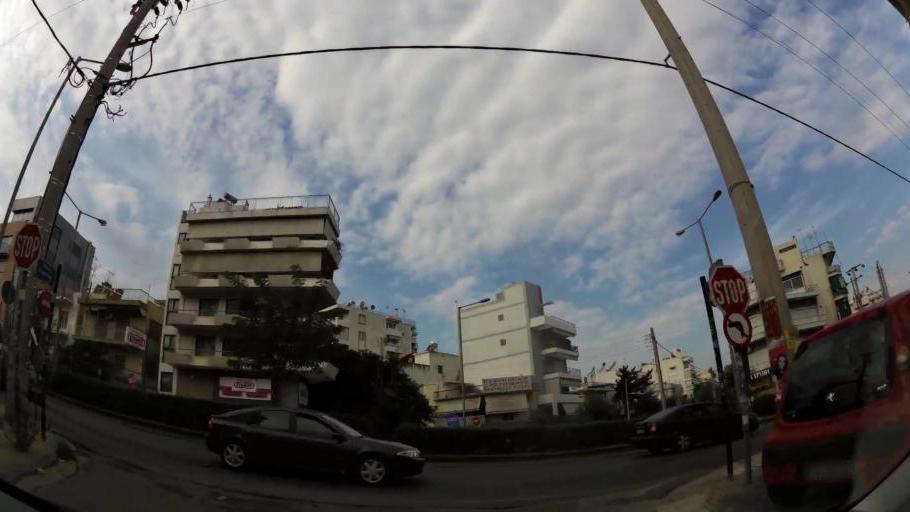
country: GR
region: Attica
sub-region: Nomarchia Athinas
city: Palaio Faliro
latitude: 37.9291
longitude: 23.7032
